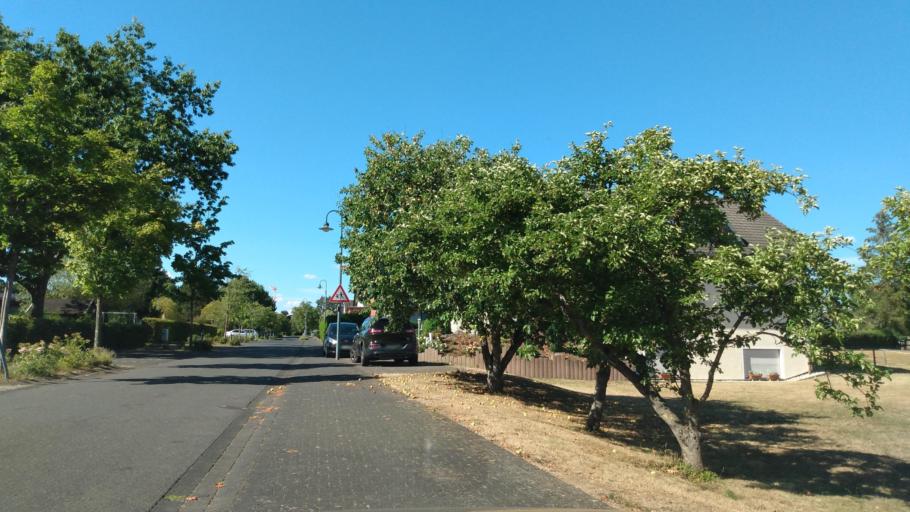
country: DE
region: Rheinland-Pfalz
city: Binsfeld
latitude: 49.9658
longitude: 6.7019
